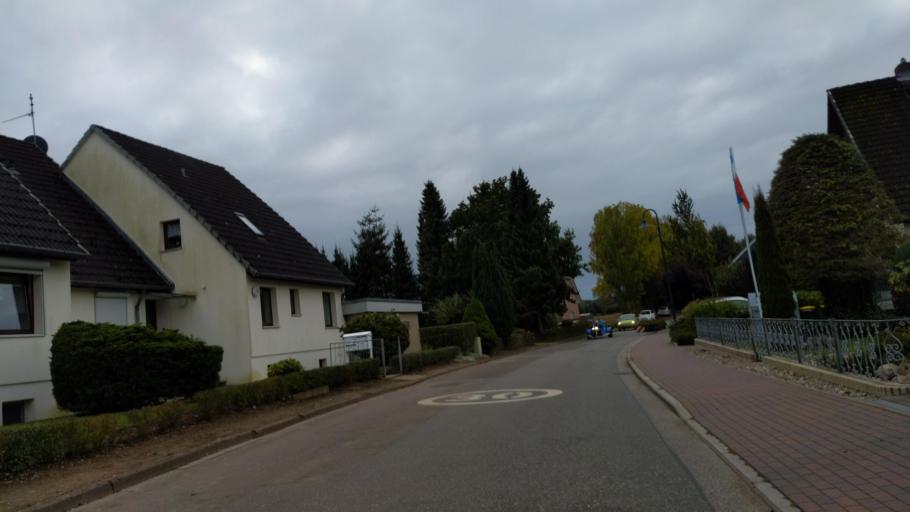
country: DE
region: Schleswig-Holstein
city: Scharbeutz
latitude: 54.0478
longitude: 10.7399
